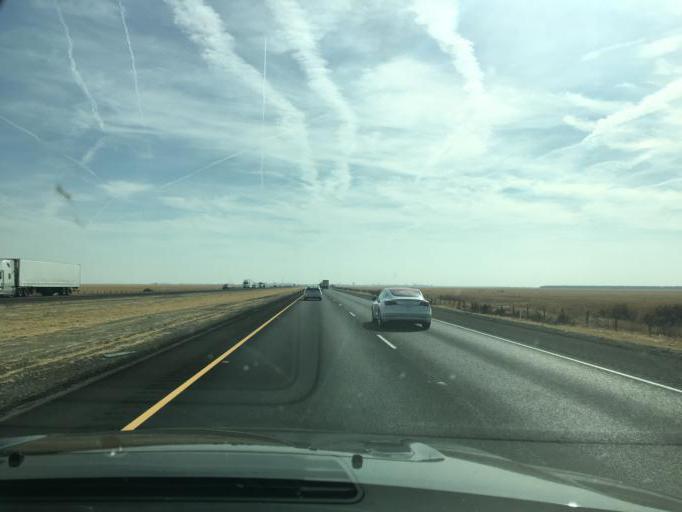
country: US
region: California
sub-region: Kern County
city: Lost Hills
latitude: 35.6461
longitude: -119.6757
